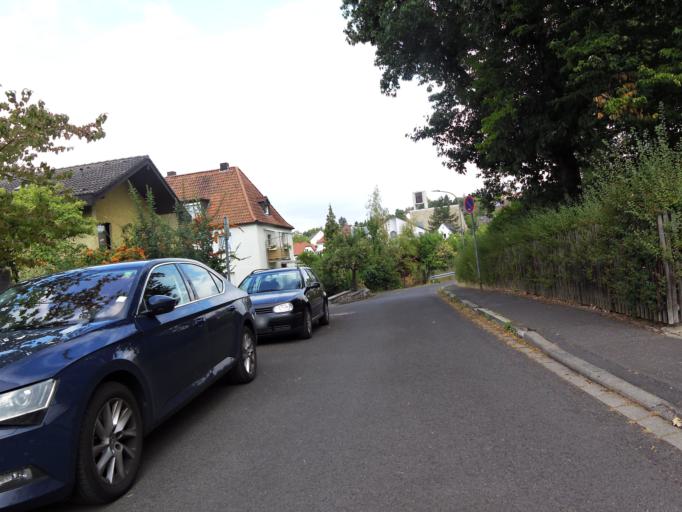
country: DE
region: Bavaria
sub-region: Regierungsbezirk Unterfranken
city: Veitshochheim
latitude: 49.8304
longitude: 9.8785
